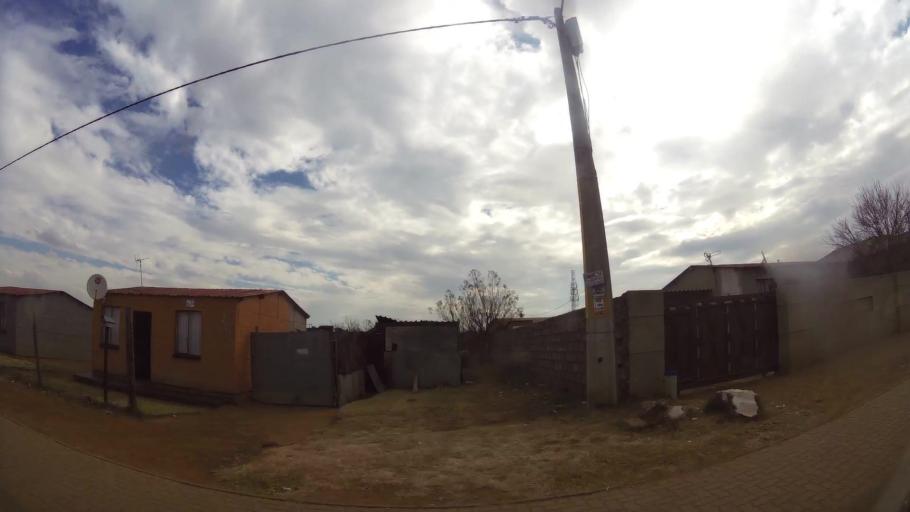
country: ZA
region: Gauteng
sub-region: Ekurhuleni Metropolitan Municipality
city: Germiston
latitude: -26.4015
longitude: 28.1478
